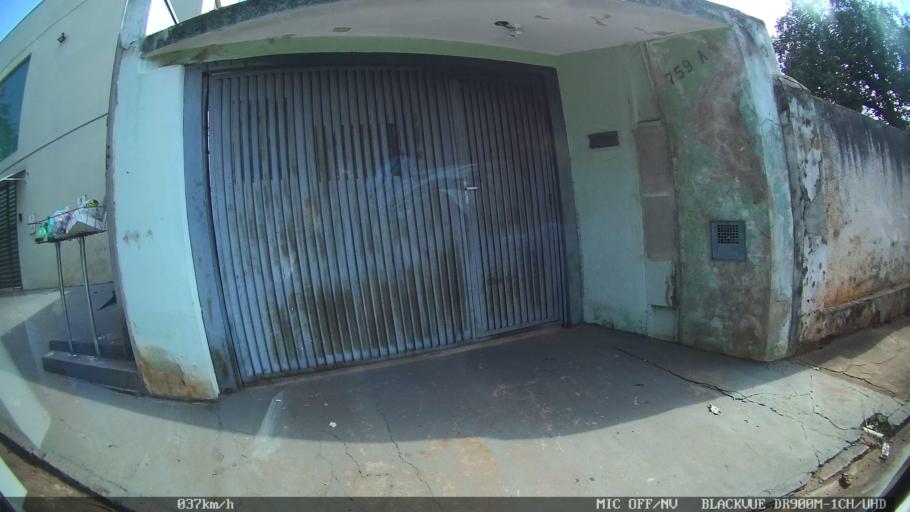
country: BR
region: Sao Paulo
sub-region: Sumare
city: Sumare
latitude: -22.8248
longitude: -47.2629
